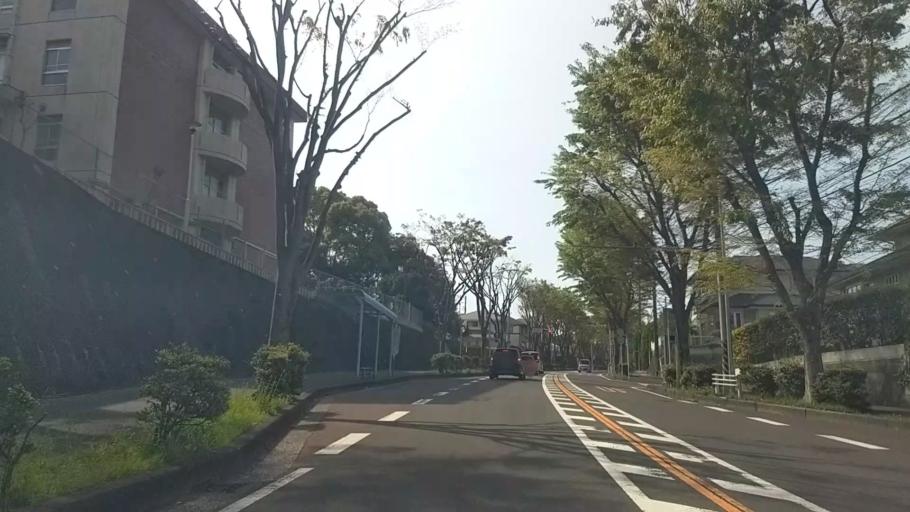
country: JP
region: Kanagawa
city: Zushi
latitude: 35.3634
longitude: 139.6107
